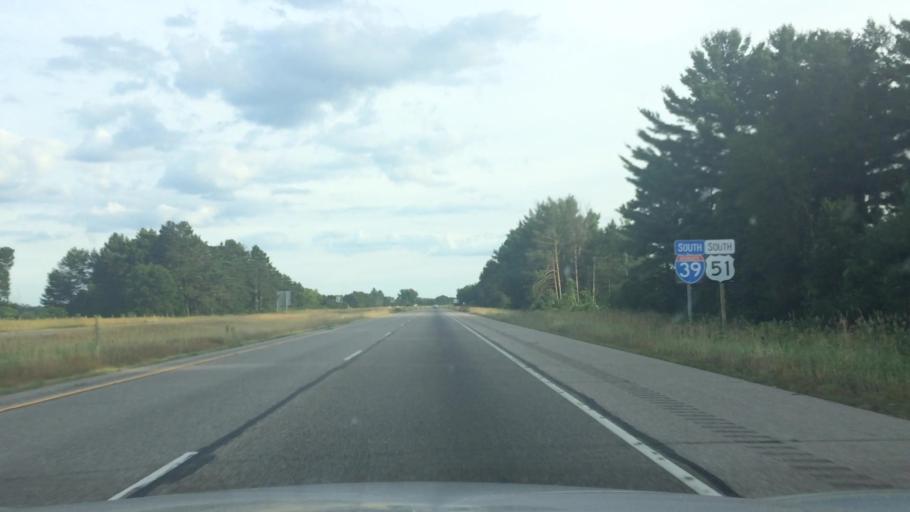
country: US
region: Wisconsin
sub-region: Portage County
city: Plover
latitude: 44.2059
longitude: -89.5238
